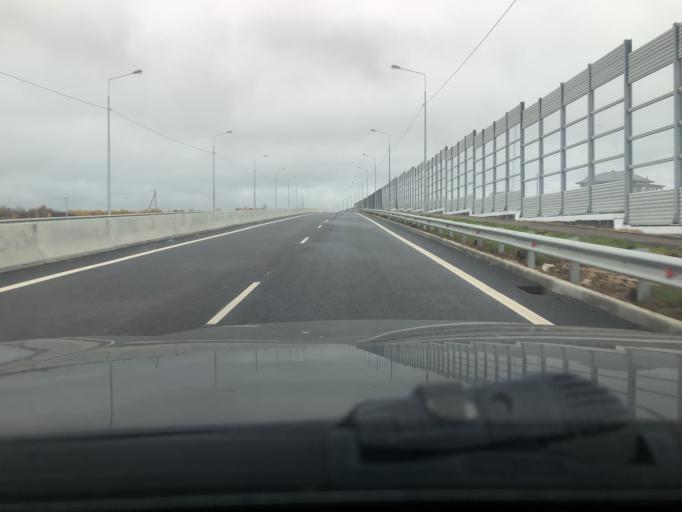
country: RU
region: Moskovskaya
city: Sergiyev Posad
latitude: 56.3097
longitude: 38.0984
